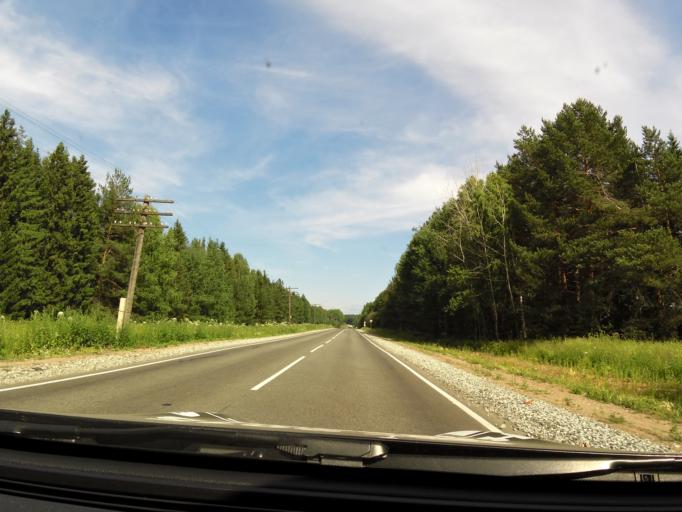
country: RU
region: Kirov
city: Slobodskoy
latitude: 58.7802
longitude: 50.4626
